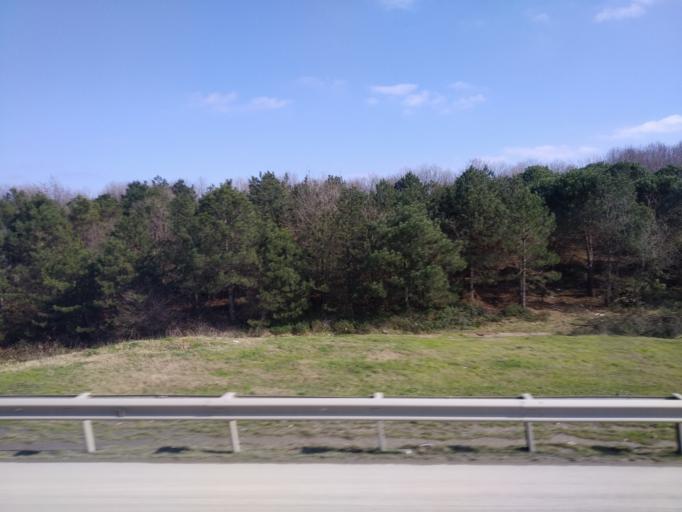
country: TR
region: Istanbul
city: Kemerburgaz
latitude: 41.1508
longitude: 28.9012
